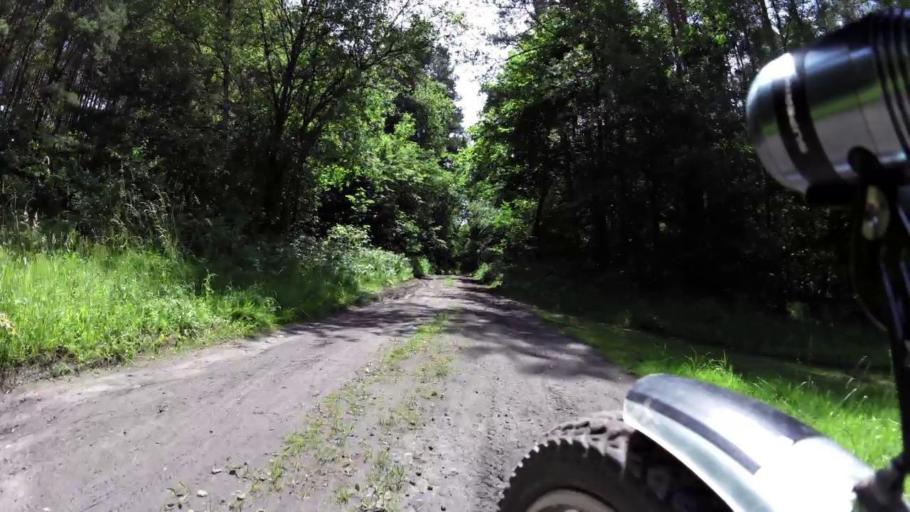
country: PL
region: West Pomeranian Voivodeship
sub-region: Powiat choszczenski
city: Choszczno
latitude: 53.1963
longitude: 15.4174
